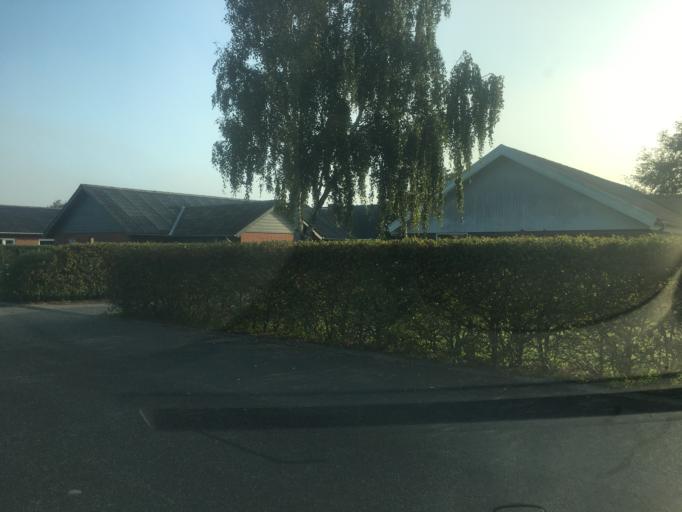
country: DK
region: South Denmark
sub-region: Tonder Kommune
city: Tonder
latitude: 54.9392
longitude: 8.8476
